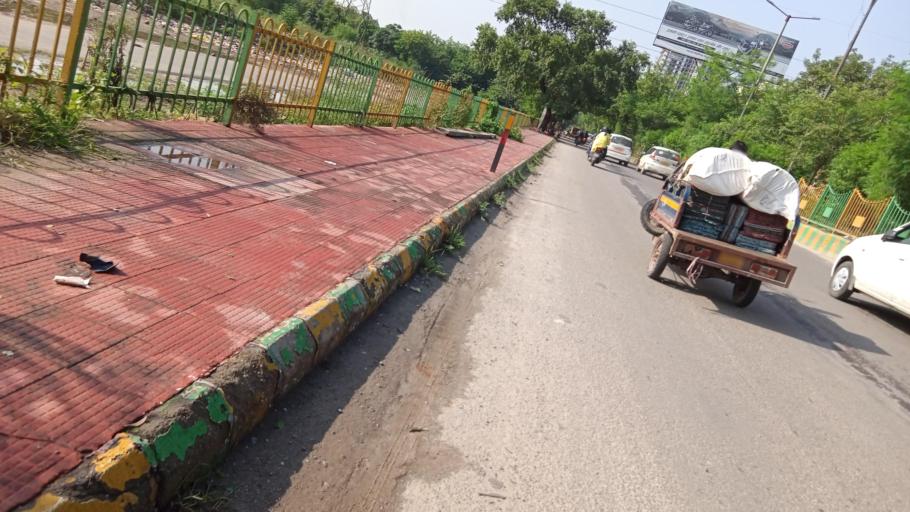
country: IN
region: Uttar Pradesh
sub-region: Ghaziabad
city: Ghaziabad
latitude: 28.6629
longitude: 77.3732
